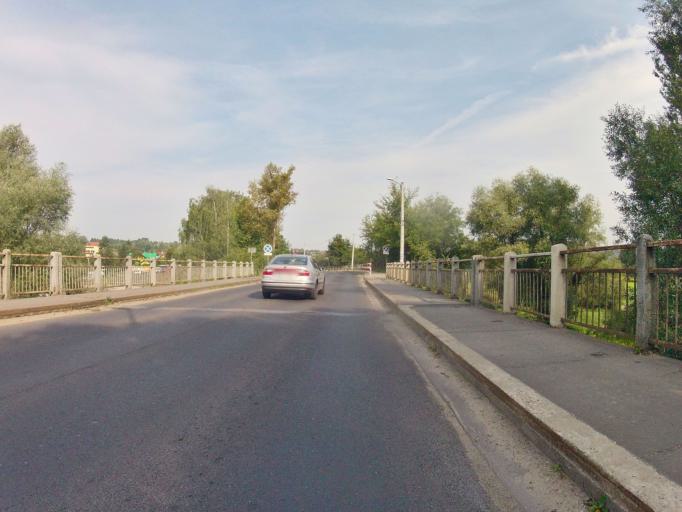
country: PL
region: Subcarpathian Voivodeship
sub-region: Powiat jasielski
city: Jaslo
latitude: 49.7514
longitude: 21.4587
